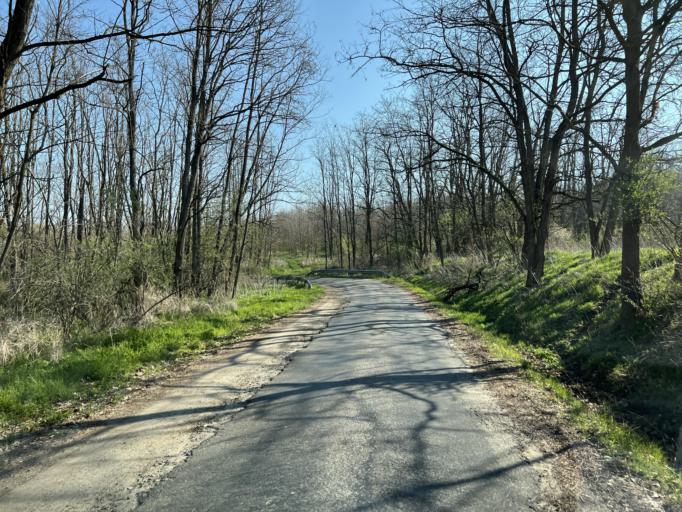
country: SK
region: Nitriansky
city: Sahy
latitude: 48.0002
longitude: 18.8213
